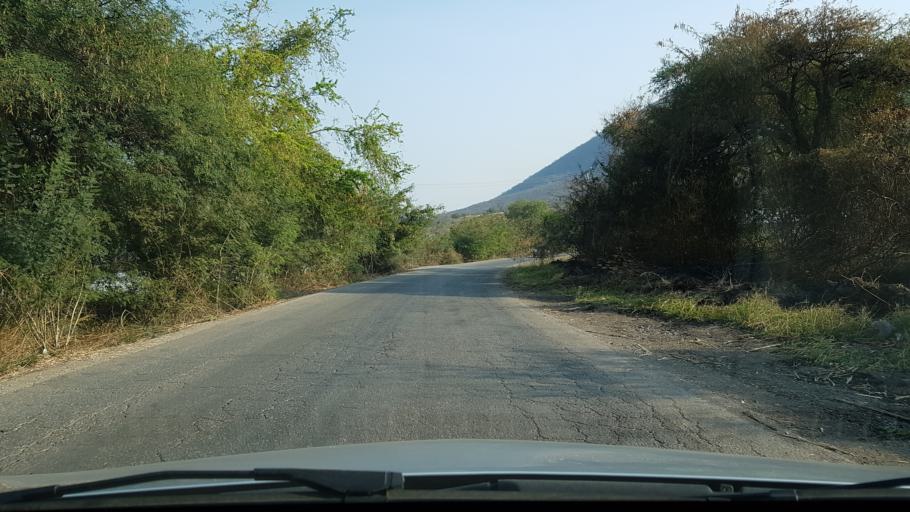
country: MX
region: Morelos
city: Tlaltizapan
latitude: 18.6812
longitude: -99.0893
